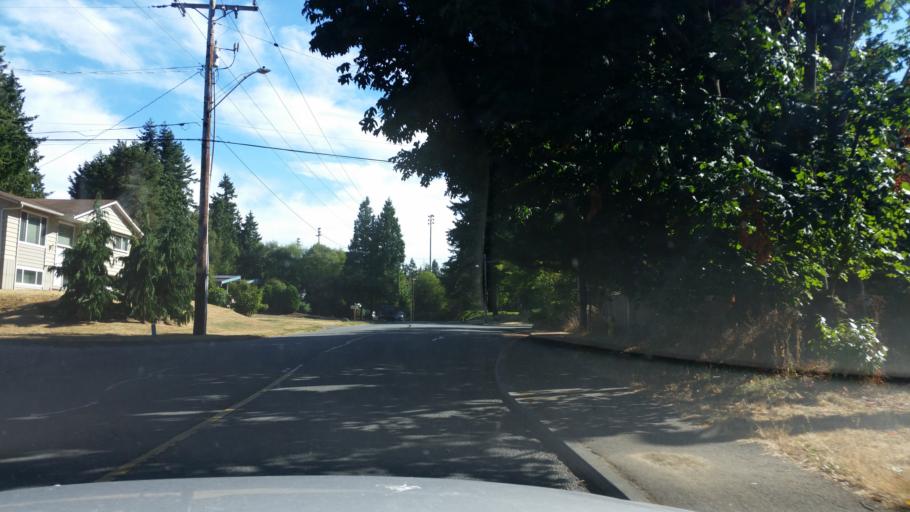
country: US
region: Washington
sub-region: Snohomish County
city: Meadowdale
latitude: 47.8503
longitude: -122.3248
